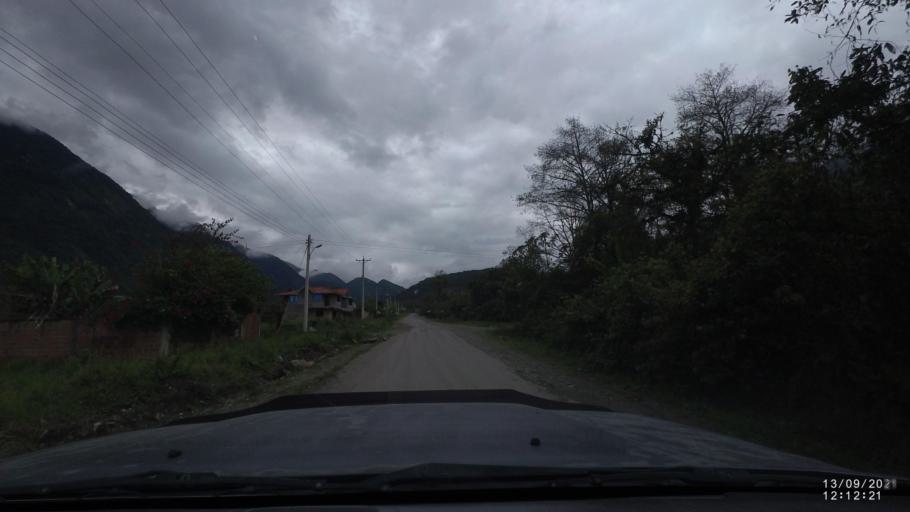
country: BO
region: Cochabamba
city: Colomi
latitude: -17.2156
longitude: -65.8238
